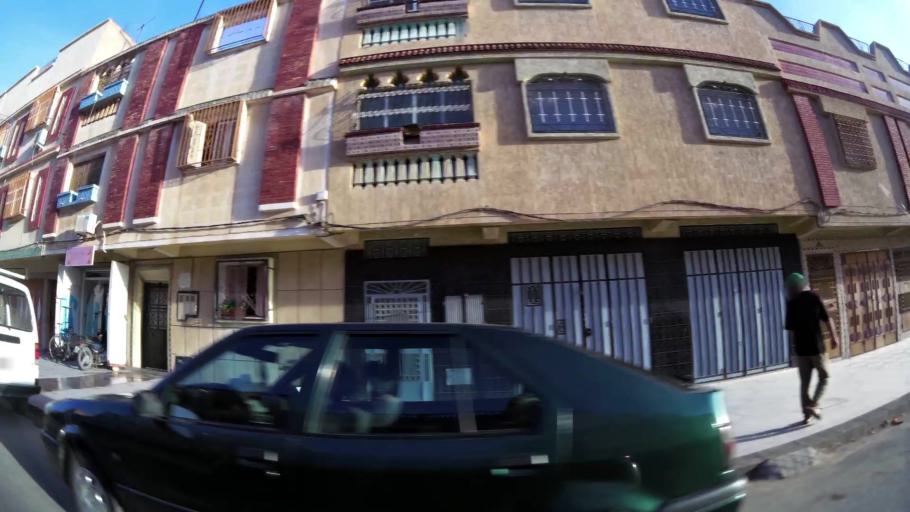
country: MA
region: Oriental
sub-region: Oujda-Angad
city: Oujda
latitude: 34.6779
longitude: -1.9017
